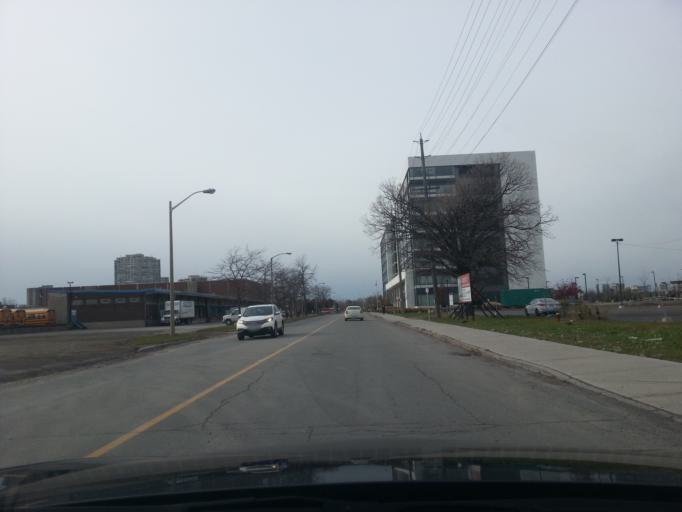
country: CA
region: Ontario
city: Ottawa
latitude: 45.4147
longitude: -75.6519
